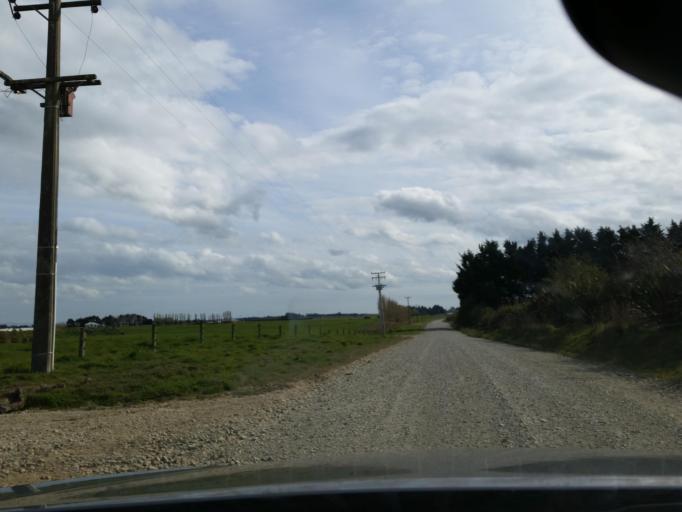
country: NZ
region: Southland
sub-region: Southland District
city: Winton
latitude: -46.2492
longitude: 168.4633
